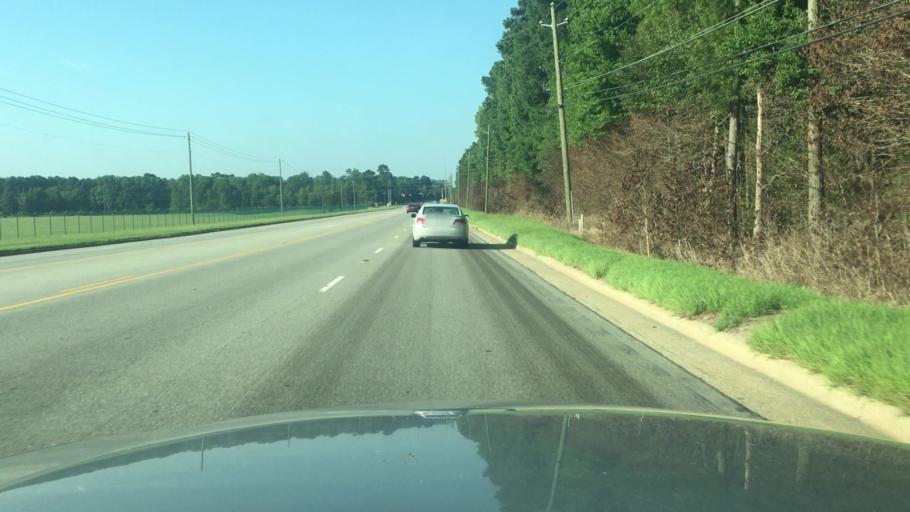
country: US
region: North Carolina
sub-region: Cumberland County
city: Eastover
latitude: 35.1727
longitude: -78.8608
